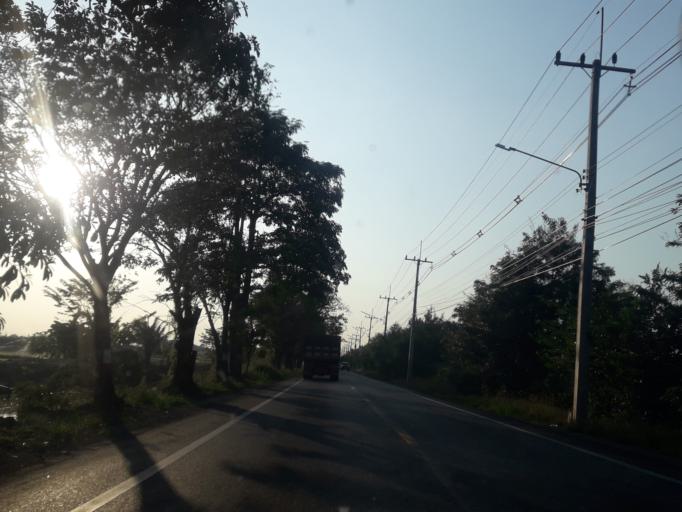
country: TH
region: Pathum Thani
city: Nong Suea
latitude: 14.1368
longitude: 100.8430
